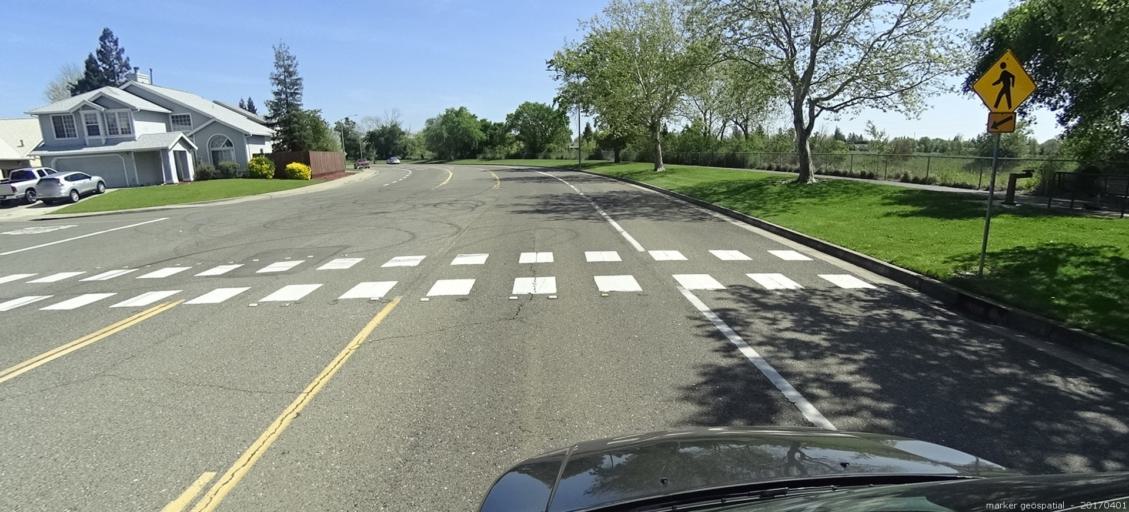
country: US
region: California
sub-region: Sacramento County
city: Laguna
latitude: 38.4422
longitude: -121.4334
